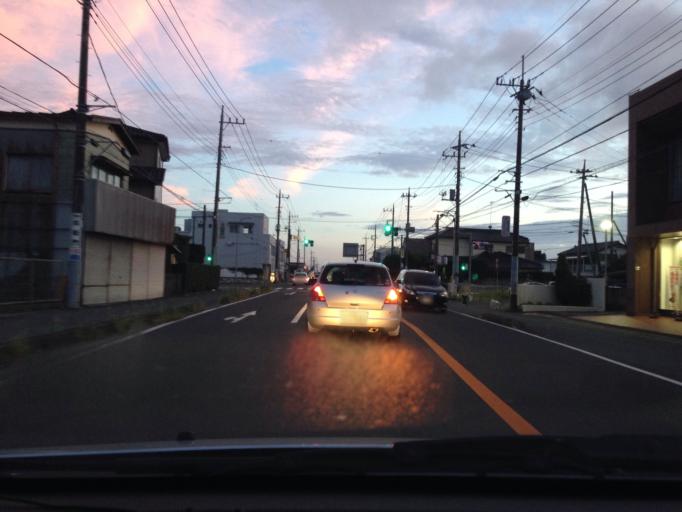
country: JP
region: Ibaraki
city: Ami
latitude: 36.0419
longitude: 140.2179
